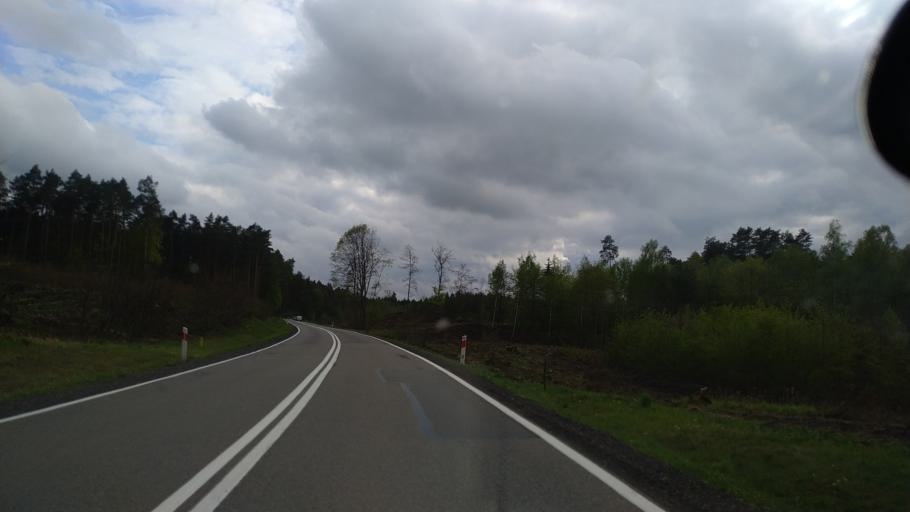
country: PL
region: Pomeranian Voivodeship
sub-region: Powiat kwidzynski
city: Ryjewo
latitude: 53.8184
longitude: 18.9796
